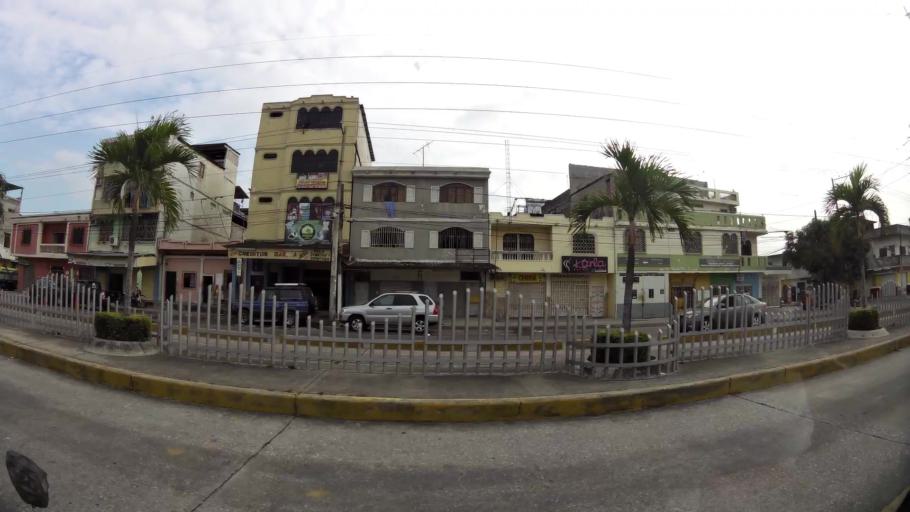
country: EC
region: Guayas
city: Guayaquil
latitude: -2.2510
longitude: -79.8877
